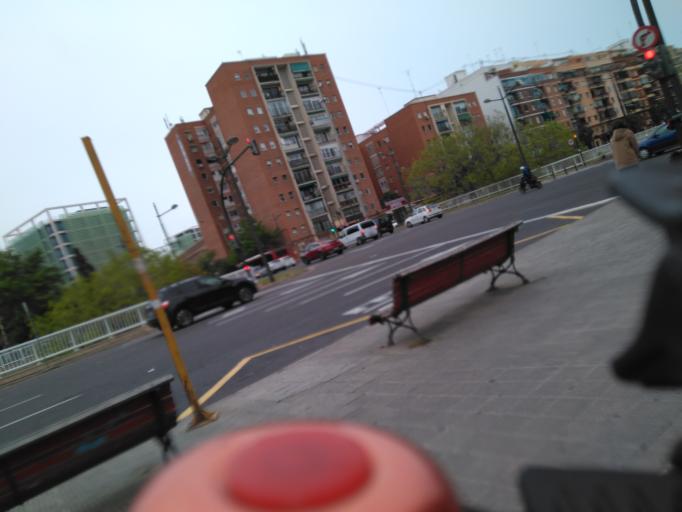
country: ES
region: Valencia
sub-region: Provincia de Valencia
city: Mislata
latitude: 39.4694
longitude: -0.4058
